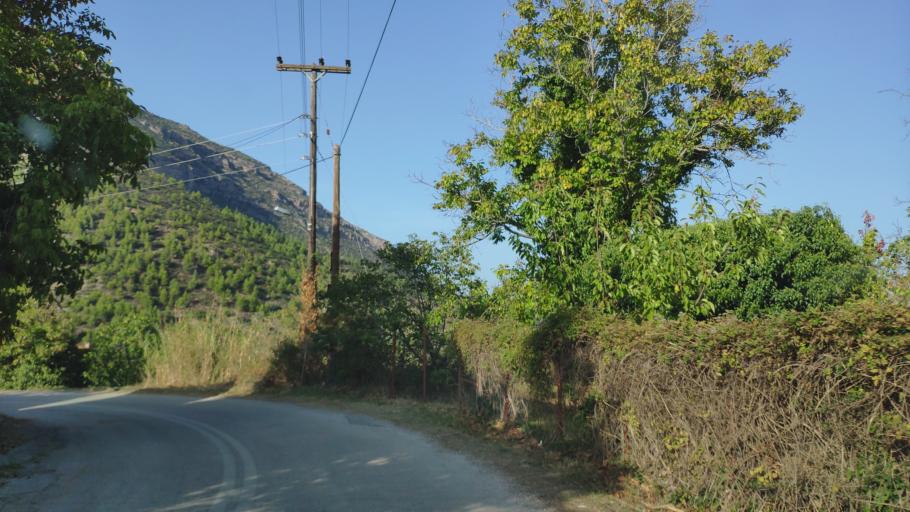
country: GR
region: West Greece
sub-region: Nomos Achaias
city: Aiyira
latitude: 38.0709
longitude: 22.3950
